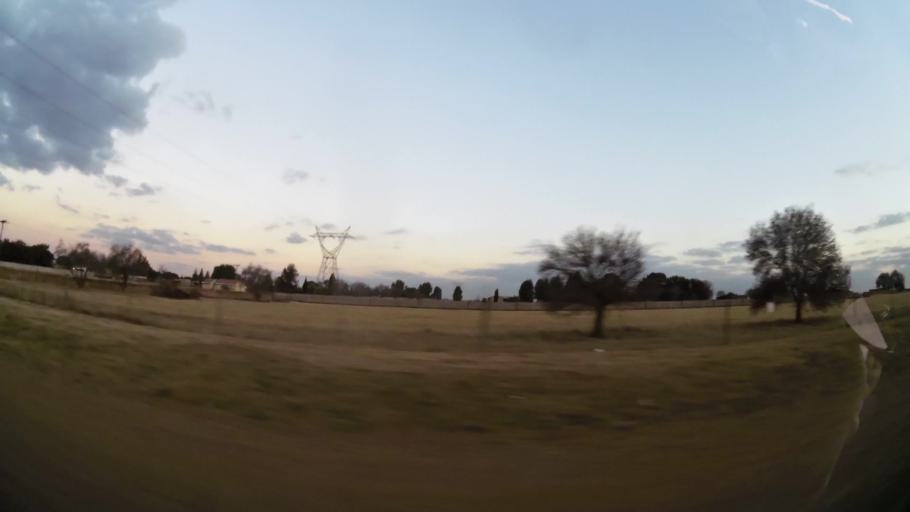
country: ZA
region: Gauteng
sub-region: West Rand District Municipality
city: Krugersdorp
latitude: -26.0710
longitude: 27.6694
